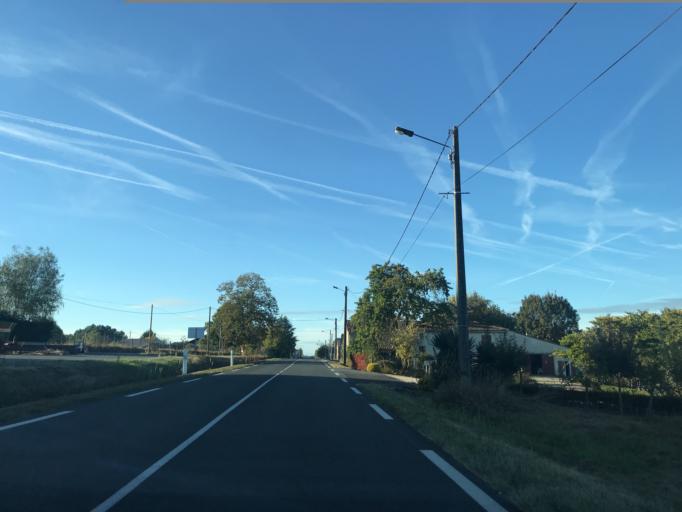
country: FR
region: Poitou-Charentes
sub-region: Departement de la Charente-Maritime
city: Montguyon
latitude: 45.1879
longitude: -0.1355
